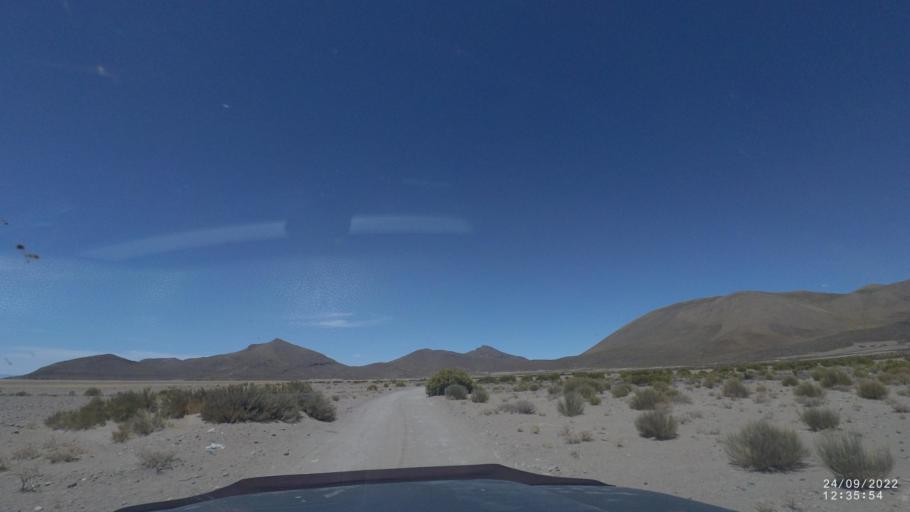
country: BO
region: Potosi
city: Colchani
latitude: -19.7842
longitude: -67.5912
